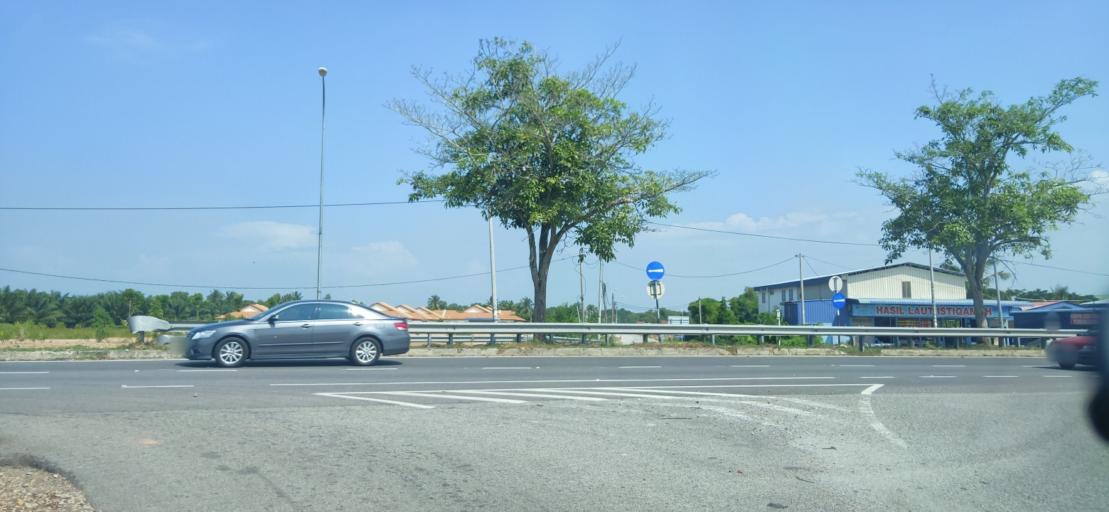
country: MY
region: Kedah
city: Sungai Petani
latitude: 5.6606
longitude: 100.4655
